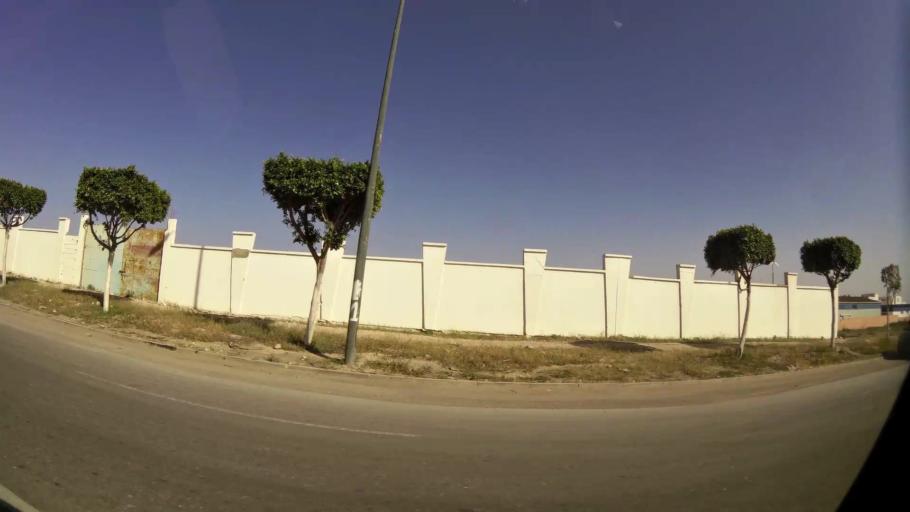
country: MA
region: Souss-Massa-Draa
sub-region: Inezgane-Ait Mellou
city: Inezgane
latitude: 30.3876
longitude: -9.5145
